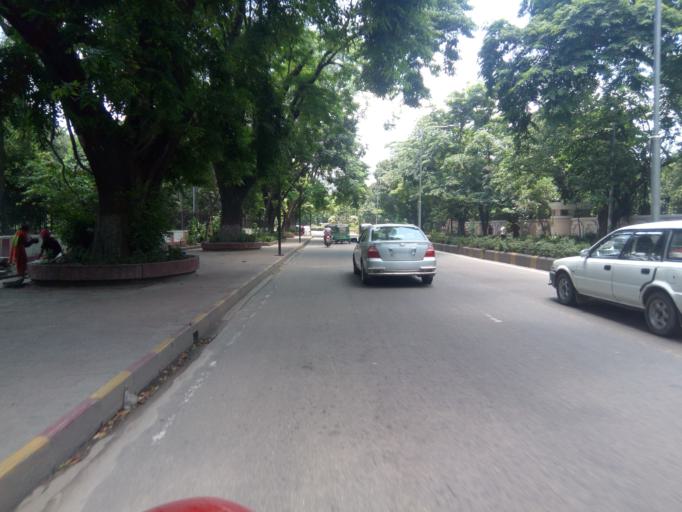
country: BD
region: Dhaka
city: Paltan
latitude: 23.7410
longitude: 90.3995
